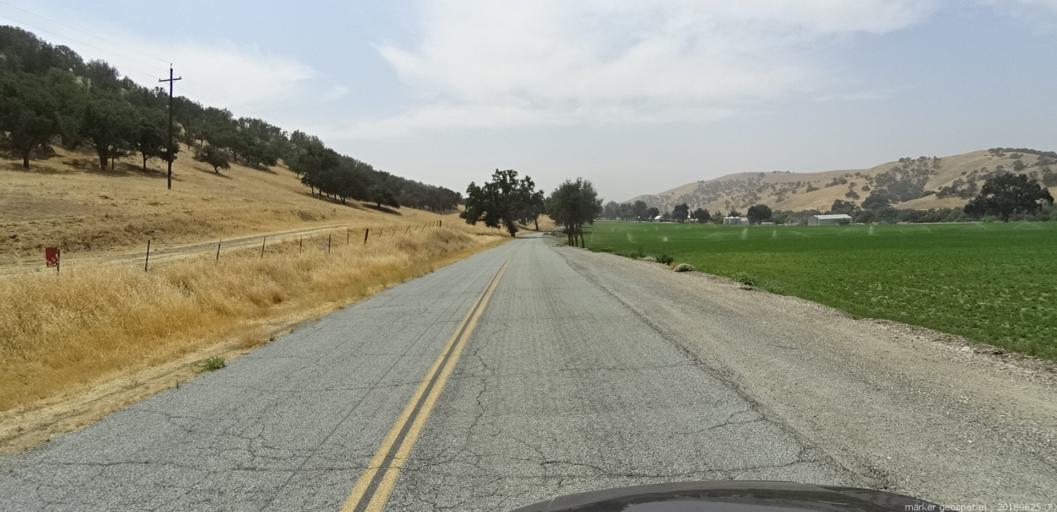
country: US
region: California
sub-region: San Luis Obispo County
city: San Miguel
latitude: 35.8139
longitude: -120.6673
